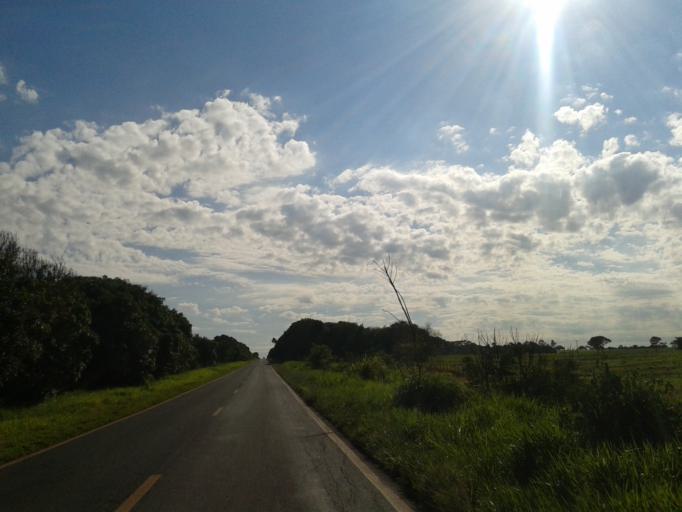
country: BR
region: Minas Gerais
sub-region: Centralina
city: Centralina
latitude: -18.7239
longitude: -49.1715
